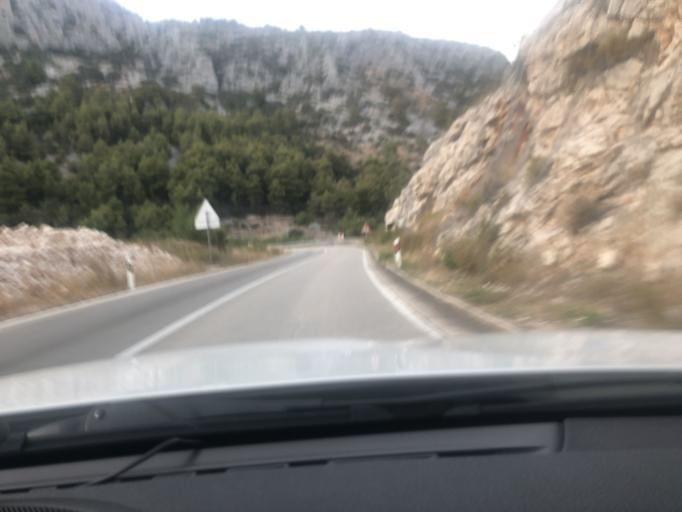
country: HR
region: Splitsko-Dalmatinska
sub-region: Grad Hvar
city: Hvar
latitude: 43.1645
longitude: 16.4895
